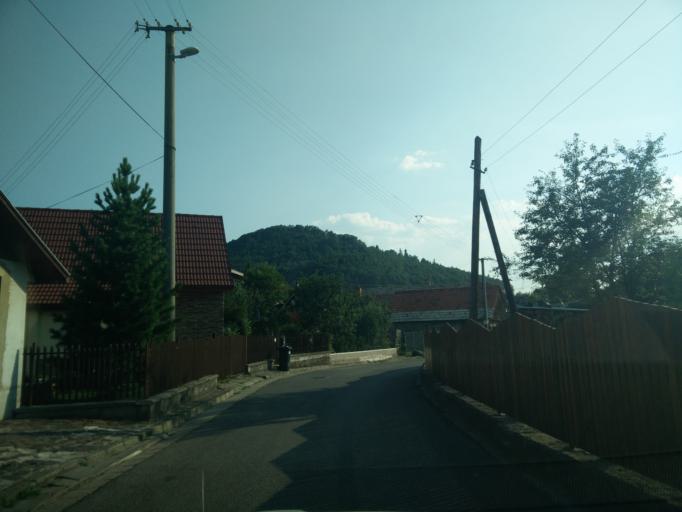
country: SK
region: Nitriansky
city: Prievidza
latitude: 48.7550
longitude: 18.6727
